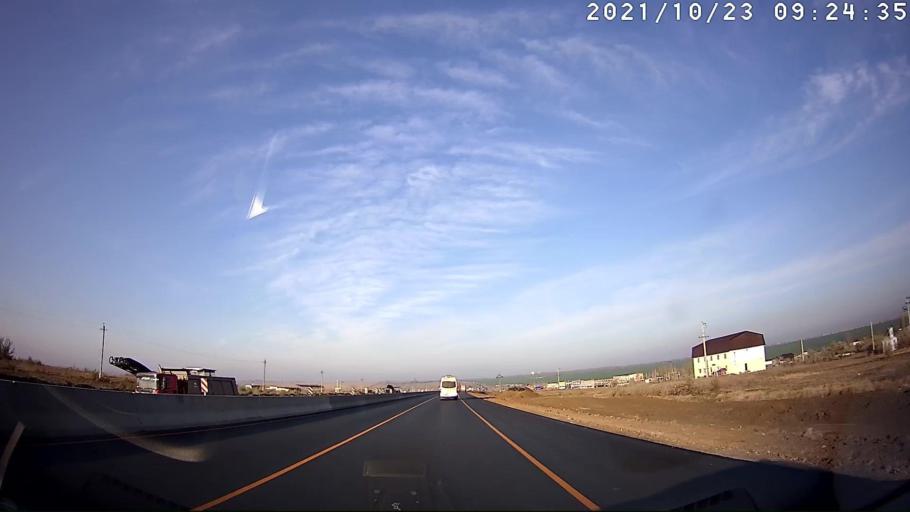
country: RU
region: Saratov
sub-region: Saratovskiy Rayon
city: Saratov
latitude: 51.6704
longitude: 45.9871
